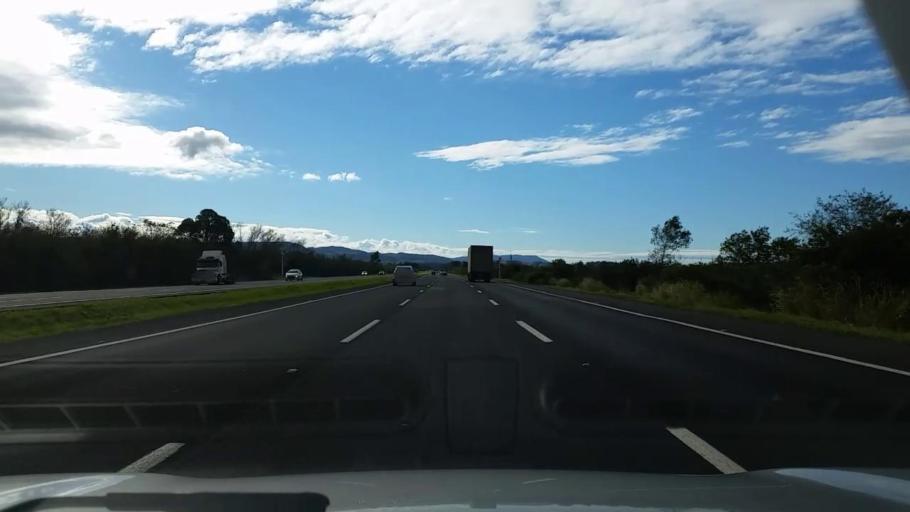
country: BR
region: Rio Grande do Sul
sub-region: Rolante
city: Rolante
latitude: -29.8828
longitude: -50.5343
